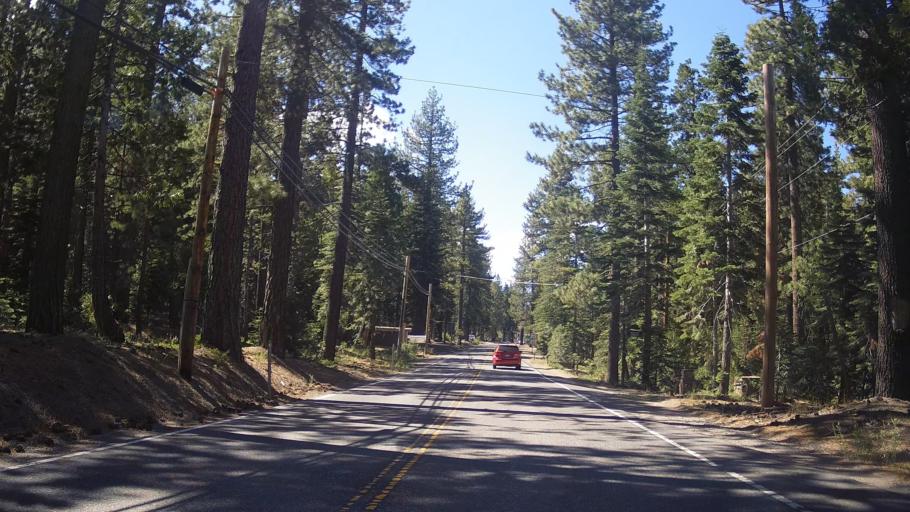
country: US
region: California
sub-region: Placer County
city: Tahoma
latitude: 39.0636
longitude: -120.1240
